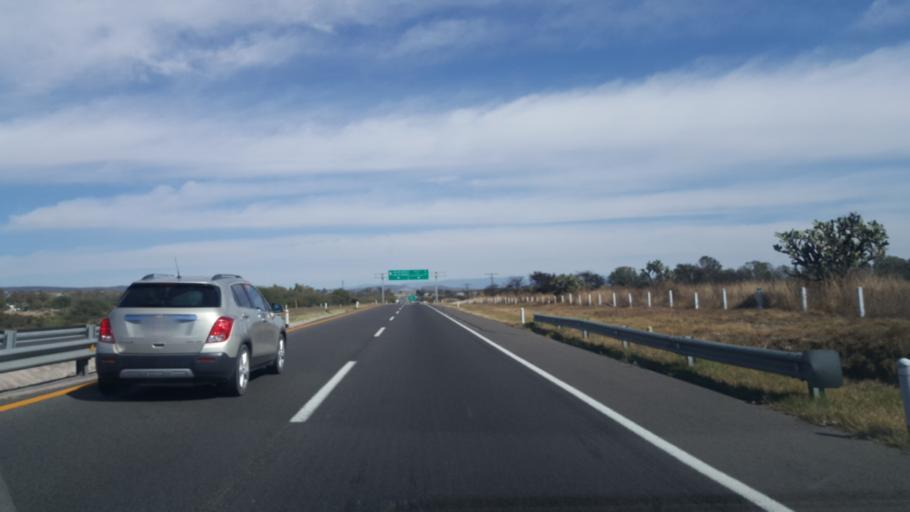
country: MX
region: Jalisco
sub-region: Lagos de Moreno
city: Cristeros [Fraccionamiento]
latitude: 21.3127
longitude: -102.0578
